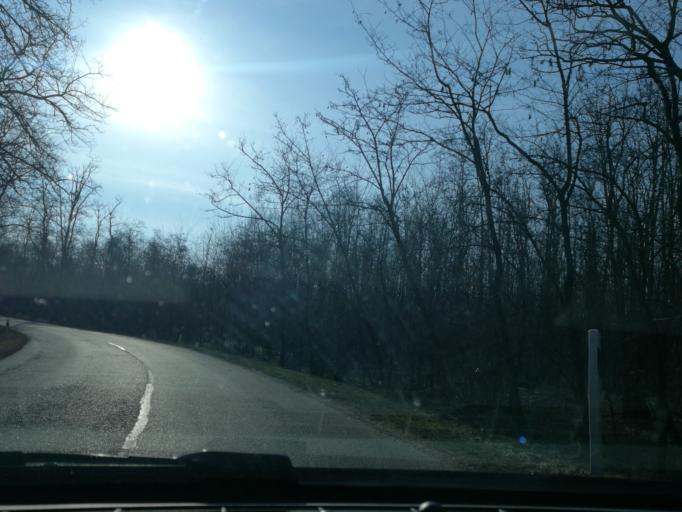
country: HU
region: Szabolcs-Szatmar-Bereg
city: Demecser
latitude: 48.0514
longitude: 21.9603
